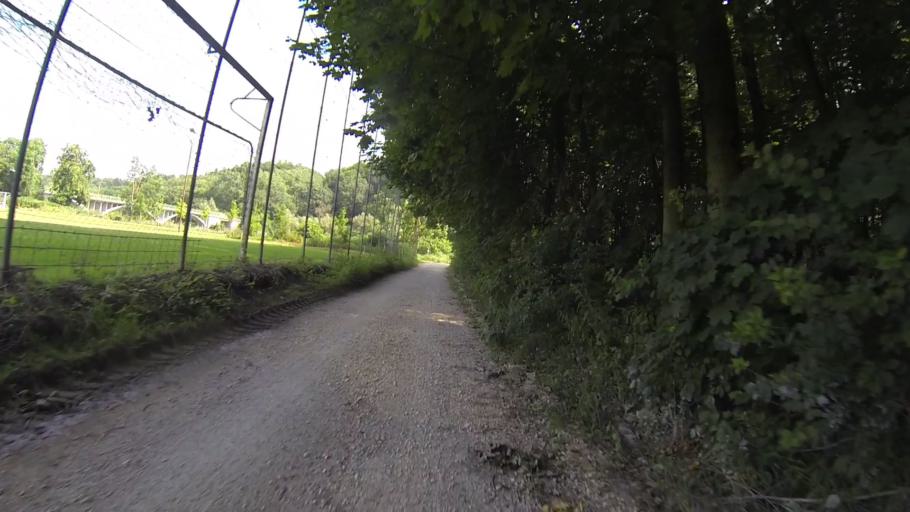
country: DE
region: Bavaria
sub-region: Swabia
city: Guenzburg
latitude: 48.4676
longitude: 10.2985
